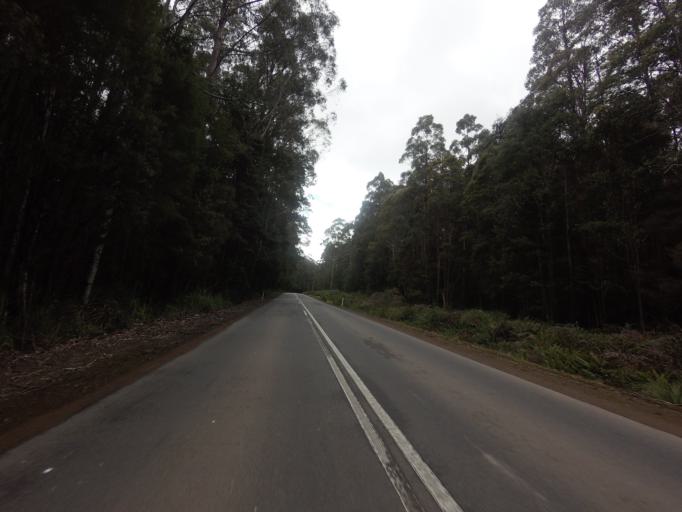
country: AU
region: Tasmania
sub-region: Huon Valley
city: Geeveston
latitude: -43.3876
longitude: 146.9625
